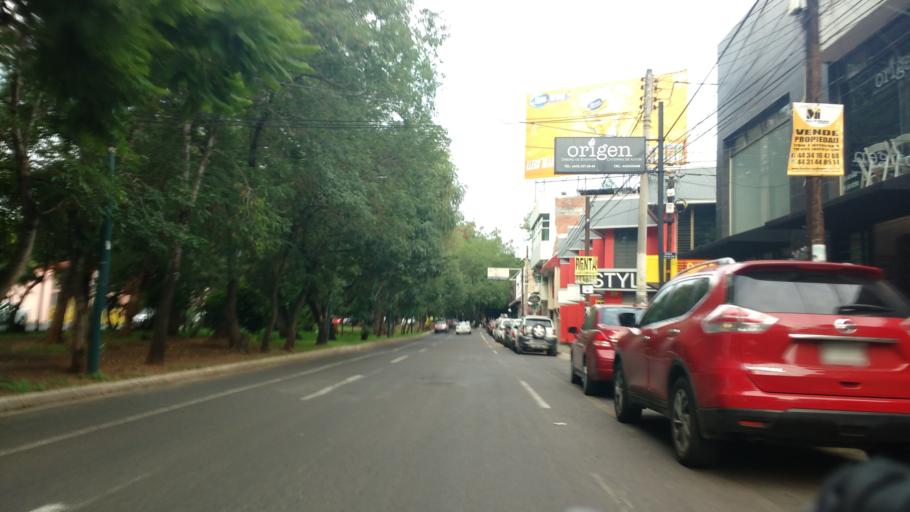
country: MX
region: Michoacan
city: Morelia
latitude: 19.6907
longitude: -101.1771
